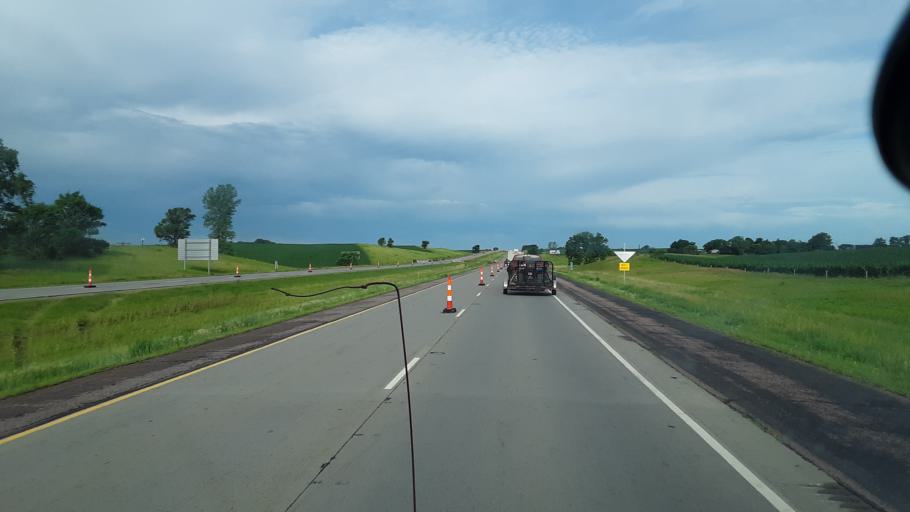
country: US
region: South Dakota
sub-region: Minnehaha County
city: Crooks
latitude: 43.6087
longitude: -96.8383
